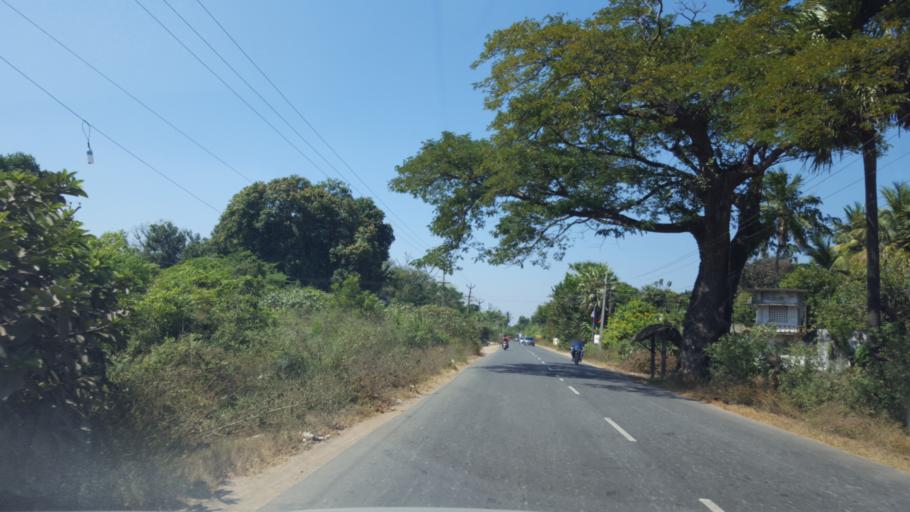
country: IN
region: Tamil Nadu
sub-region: Kancheepuram
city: Chengalpattu
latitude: 12.7237
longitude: 79.9523
